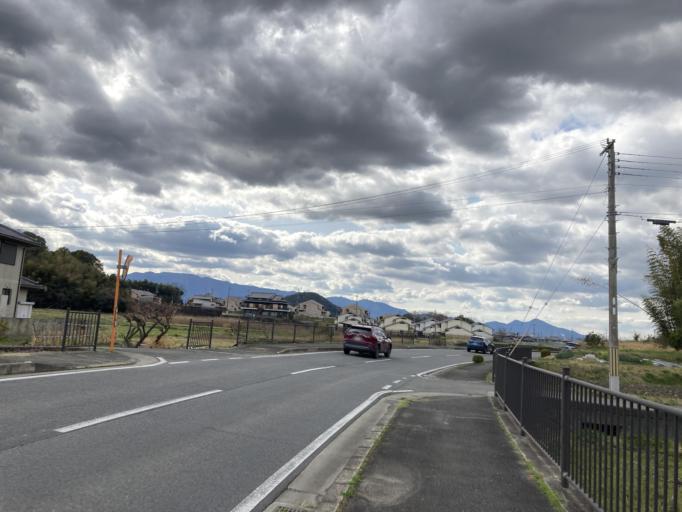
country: JP
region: Nara
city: Kashihara-shi
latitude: 34.4949
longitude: 135.8107
